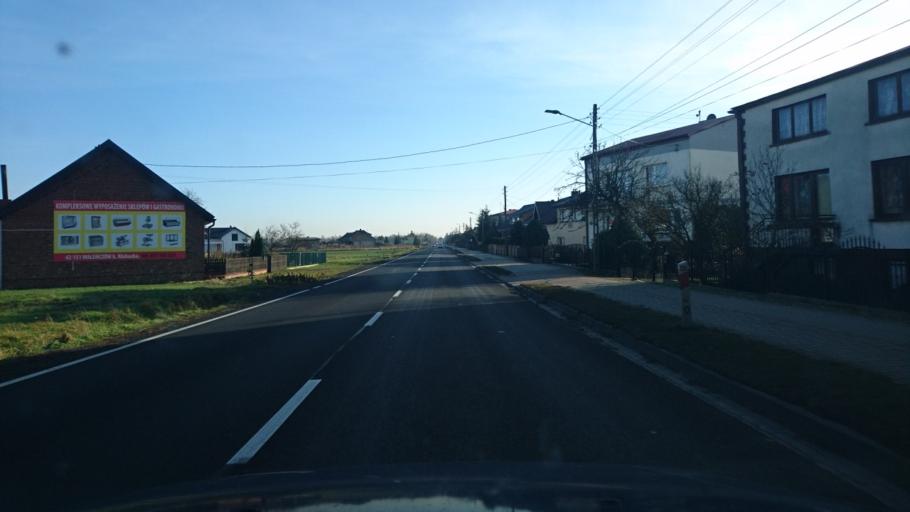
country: PL
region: Silesian Voivodeship
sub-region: Powiat klobucki
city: Starokrzepice
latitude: 51.0006
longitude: 18.6658
